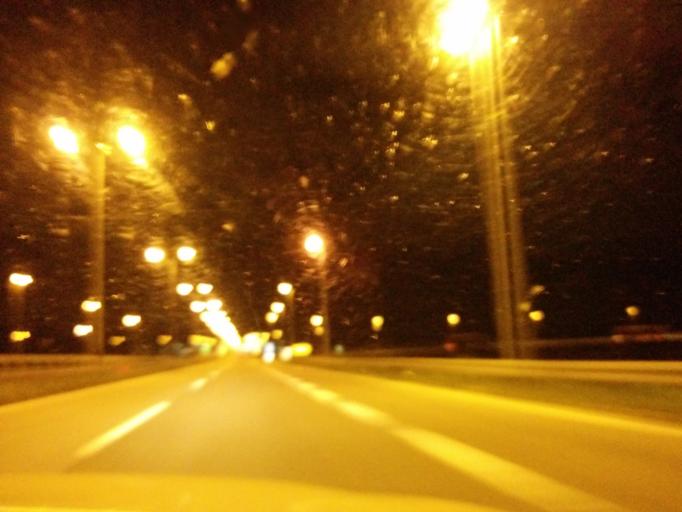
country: RS
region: Autonomna Pokrajina Vojvodina
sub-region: Sremski Okrug
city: Sid
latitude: 45.0481
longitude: 19.2089
